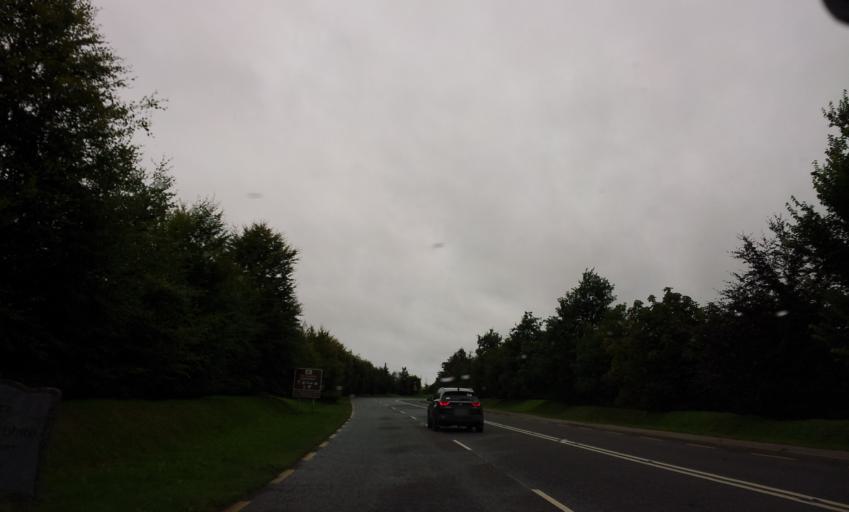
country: IE
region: Munster
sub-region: County Cork
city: Mitchelstown
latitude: 52.2469
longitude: -8.4181
